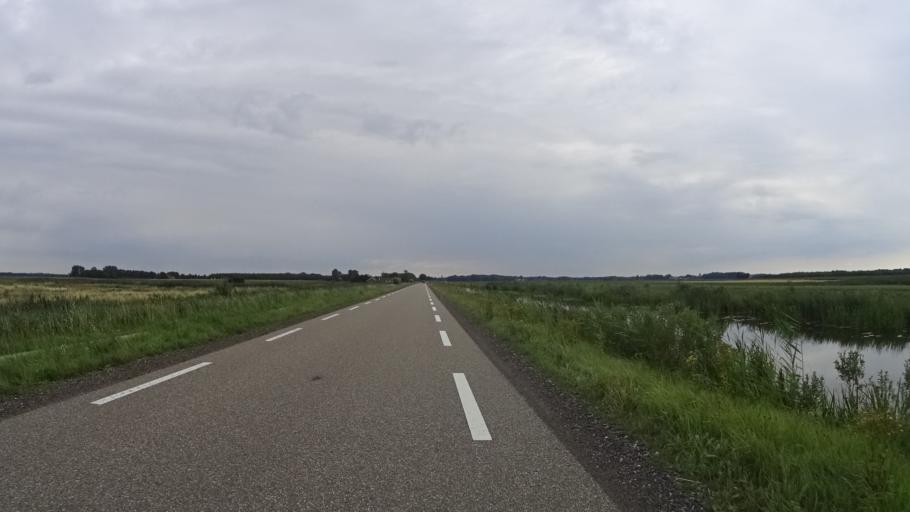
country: NL
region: Groningen
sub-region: Gemeente Slochteren
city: Slochteren
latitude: 53.2297
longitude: 6.7654
